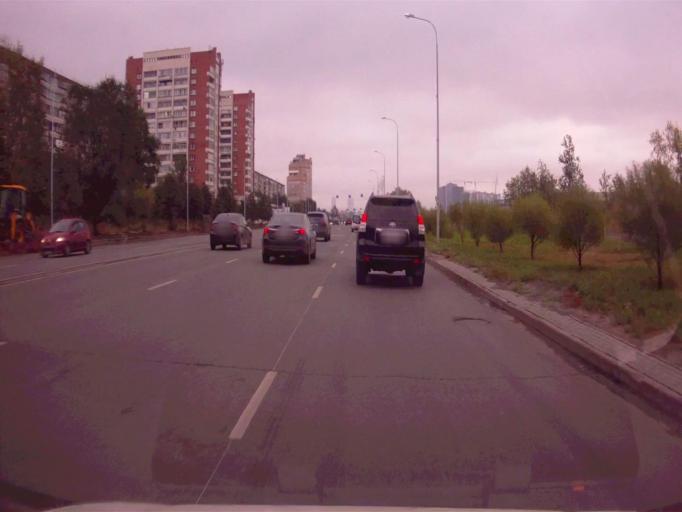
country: RU
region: Chelyabinsk
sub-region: Gorod Chelyabinsk
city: Chelyabinsk
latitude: 55.1740
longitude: 61.3476
